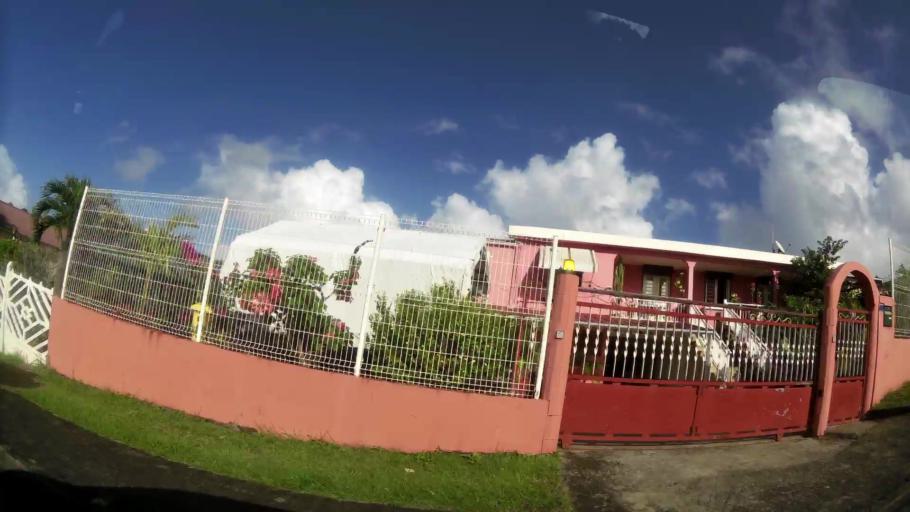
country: MQ
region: Martinique
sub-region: Martinique
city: Ducos
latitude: 14.5733
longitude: -60.9788
